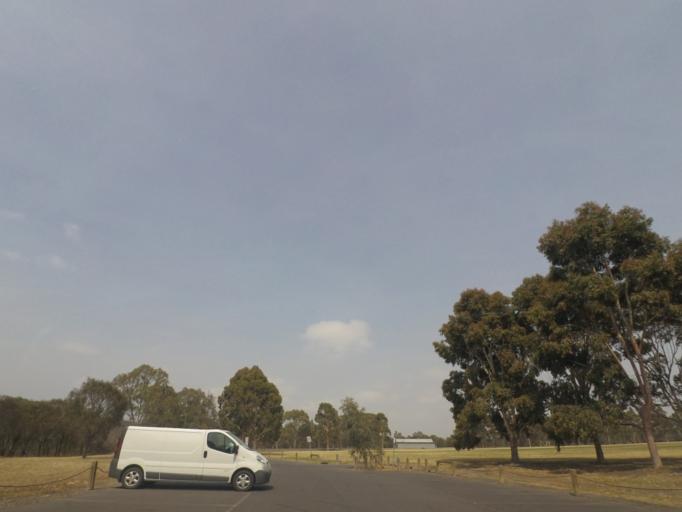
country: AU
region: Victoria
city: Abbotsford
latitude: -37.7951
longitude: 145.0087
